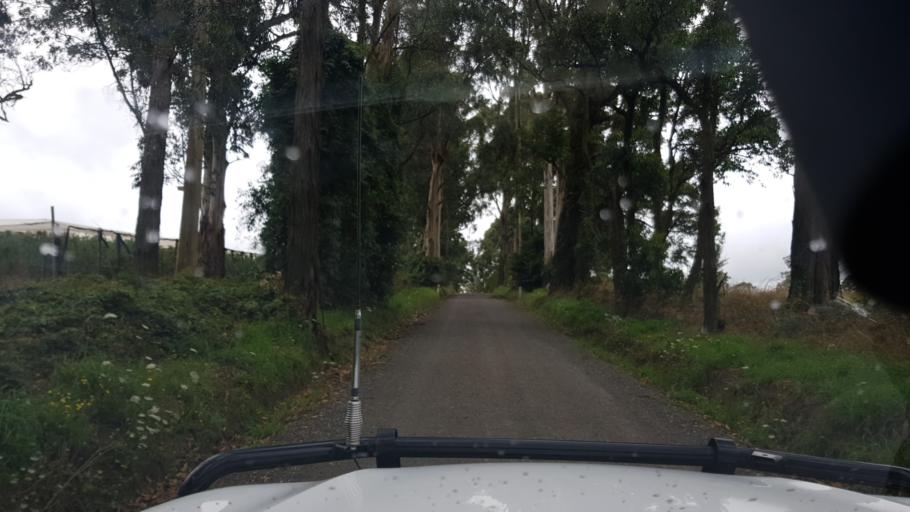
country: AU
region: Victoria
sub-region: Baw Baw
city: Warragul
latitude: -38.1855
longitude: 145.8810
